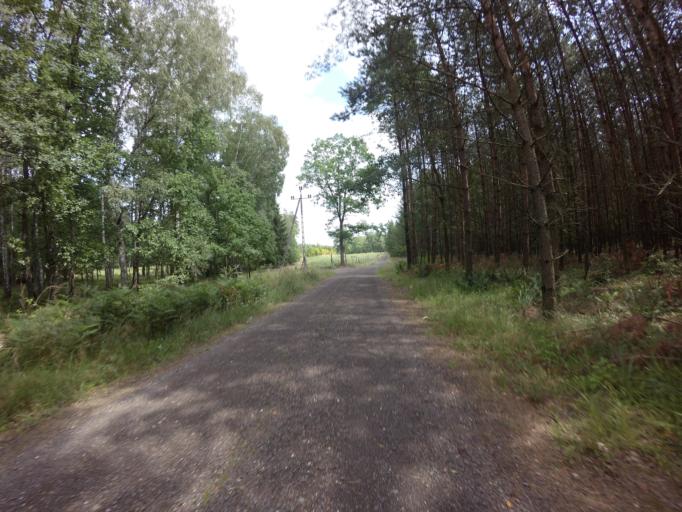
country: PL
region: Kujawsko-Pomorskie
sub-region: Powiat bydgoski
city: Koronowo
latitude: 53.3784
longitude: 17.9827
